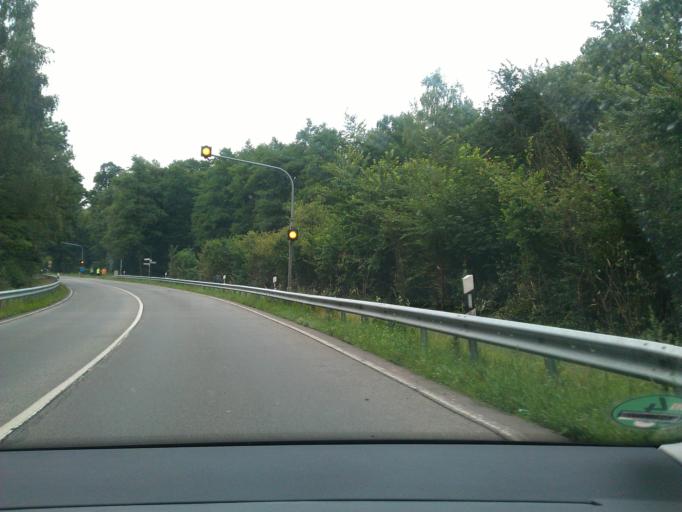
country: DE
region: North Rhine-Westphalia
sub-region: Regierungsbezirk Koln
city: Aachen
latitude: 50.7413
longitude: 6.1078
